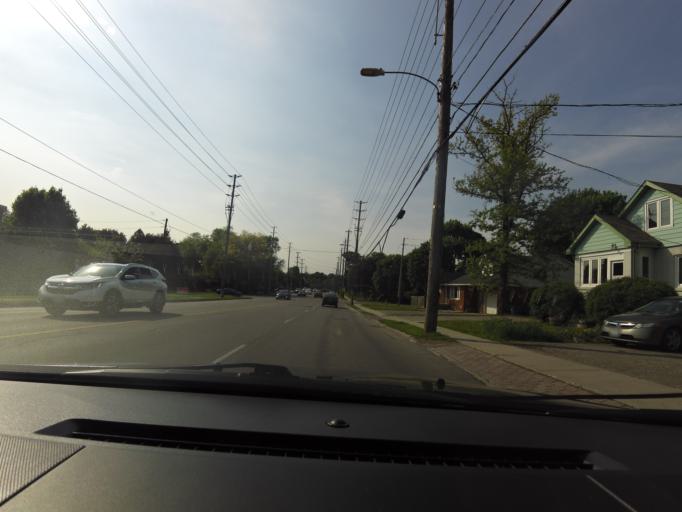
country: CA
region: Ontario
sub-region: Wellington County
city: Guelph
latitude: 43.5310
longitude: -80.2493
